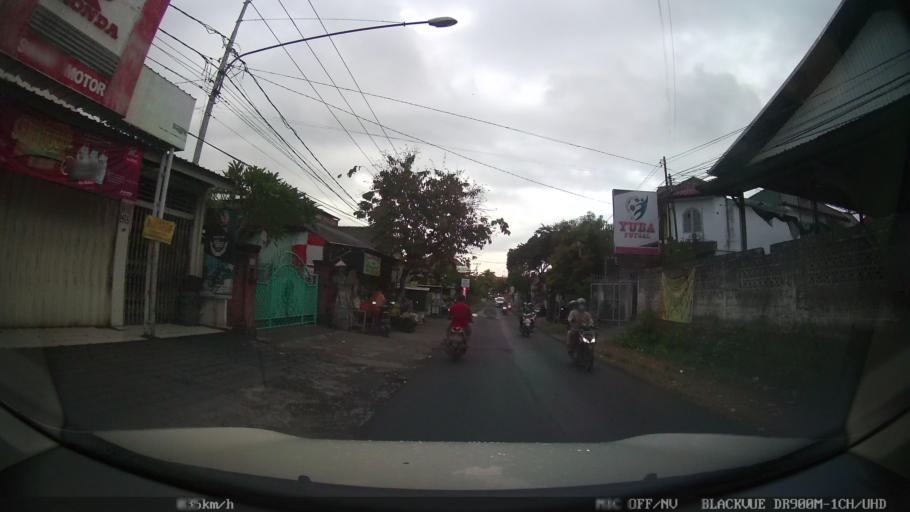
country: ID
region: Bali
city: Banjar Kertajiwa
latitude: -8.6275
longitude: 115.2632
